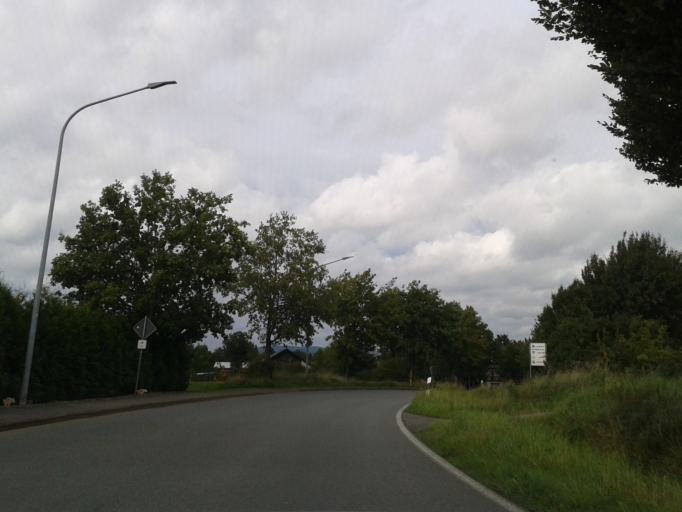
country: DE
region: North Rhine-Westphalia
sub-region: Regierungsbezirk Detmold
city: Lemgo
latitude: 52.0094
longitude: 8.9261
